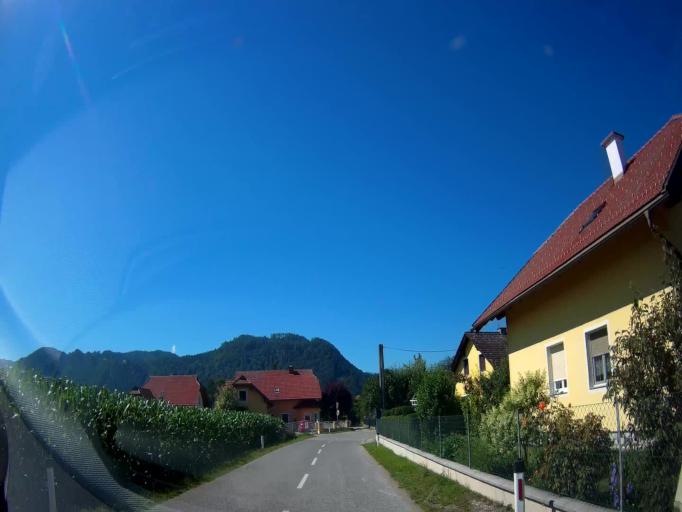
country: AT
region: Carinthia
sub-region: Politischer Bezirk Klagenfurt Land
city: Grafenstein
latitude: 46.6160
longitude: 14.4517
